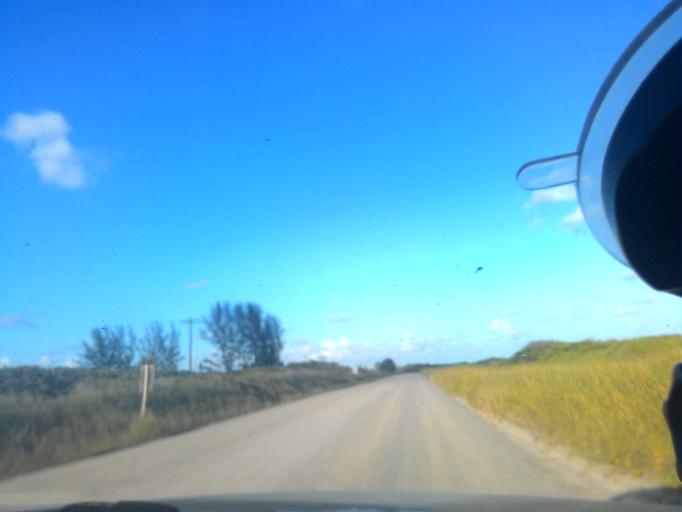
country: BR
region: Sao Paulo
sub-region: Pariquera-Acu
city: Pariquera Acu
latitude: -24.8708
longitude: -47.7227
